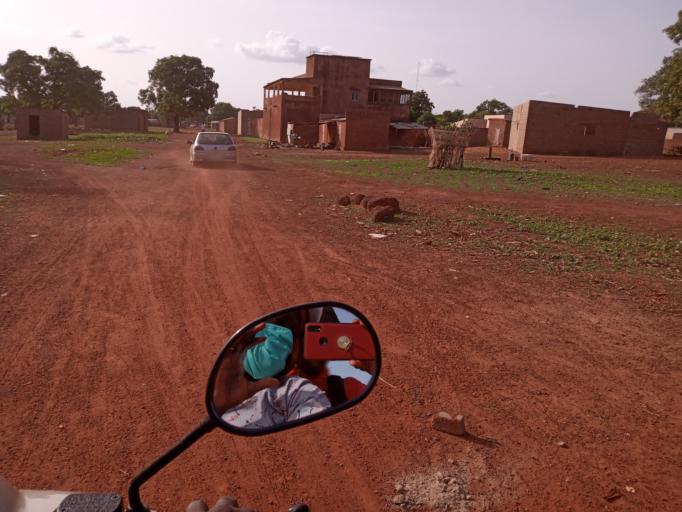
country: ML
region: Koulikoro
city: Kangaba
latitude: 12.1347
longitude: -8.2332
